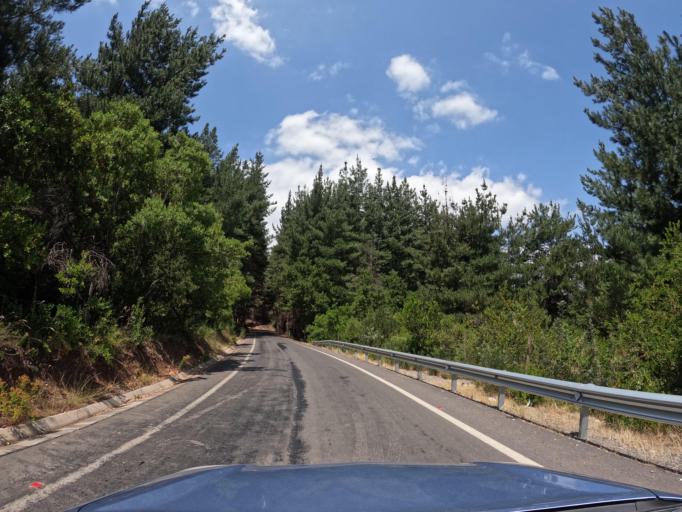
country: CL
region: Maule
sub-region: Provincia de Curico
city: Molina
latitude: -35.1754
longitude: -71.0984
